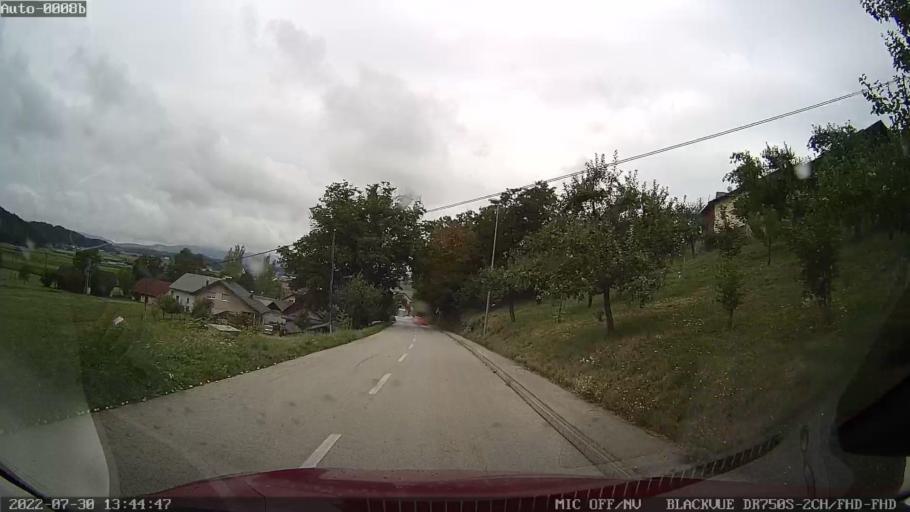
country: SI
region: Ivancna Gorica
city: Sentvid pri Sticni
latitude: 45.9199
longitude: 14.8914
